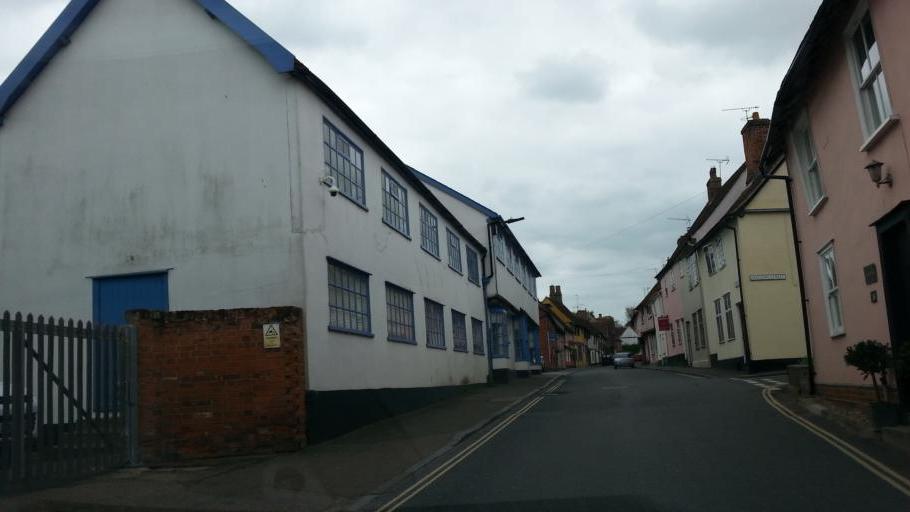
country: GB
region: England
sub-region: Suffolk
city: Lavenham
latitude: 52.1070
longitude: 0.7997
